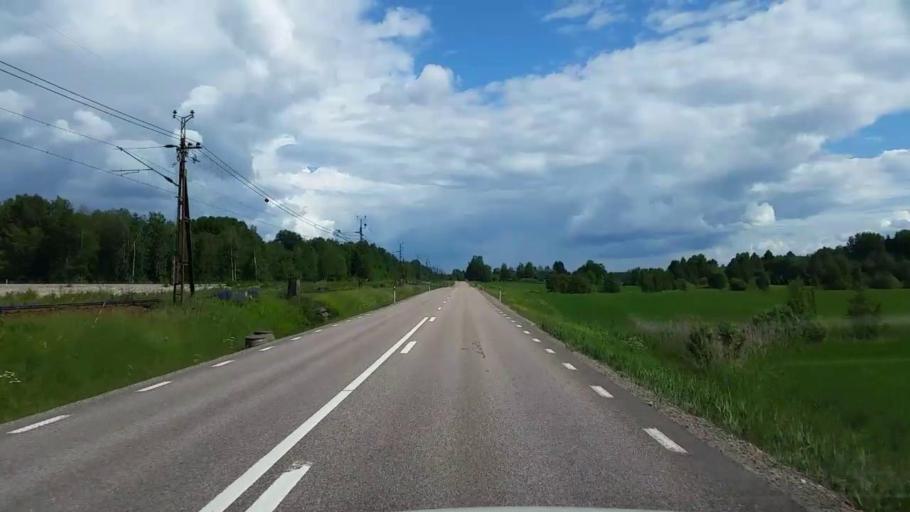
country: SE
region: Dalarna
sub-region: Avesta Kommun
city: Avesta
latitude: 60.1536
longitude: 16.2468
